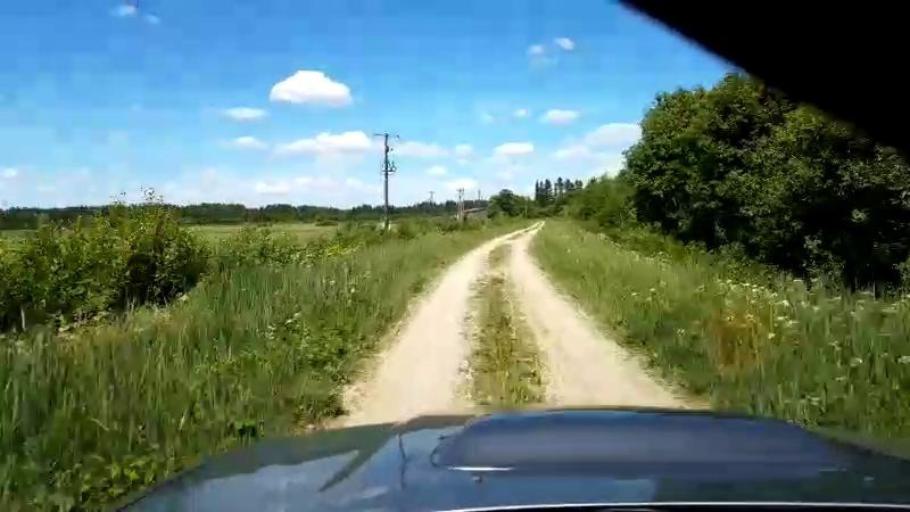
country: EE
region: Paernumaa
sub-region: Halinga vald
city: Parnu-Jaagupi
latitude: 58.5407
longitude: 24.5311
